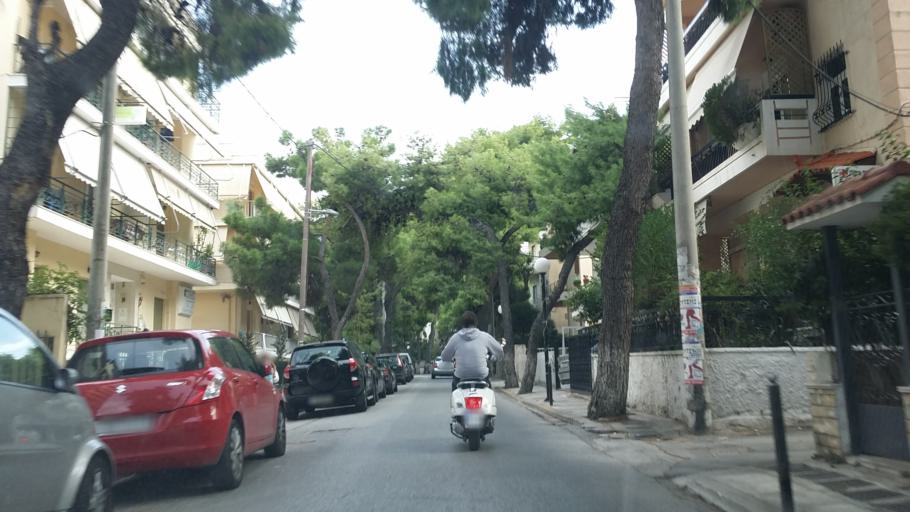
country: GR
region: Attica
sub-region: Nomarchia Athinas
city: Irakleio
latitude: 38.0490
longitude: 23.7651
